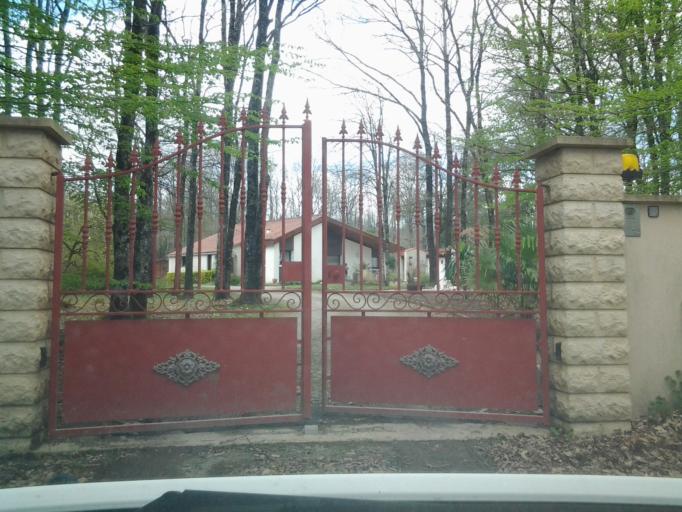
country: FR
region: Pays de la Loire
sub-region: Departement de la Vendee
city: Dompierre-sur-Yon
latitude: 46.7061
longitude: -1.3676
